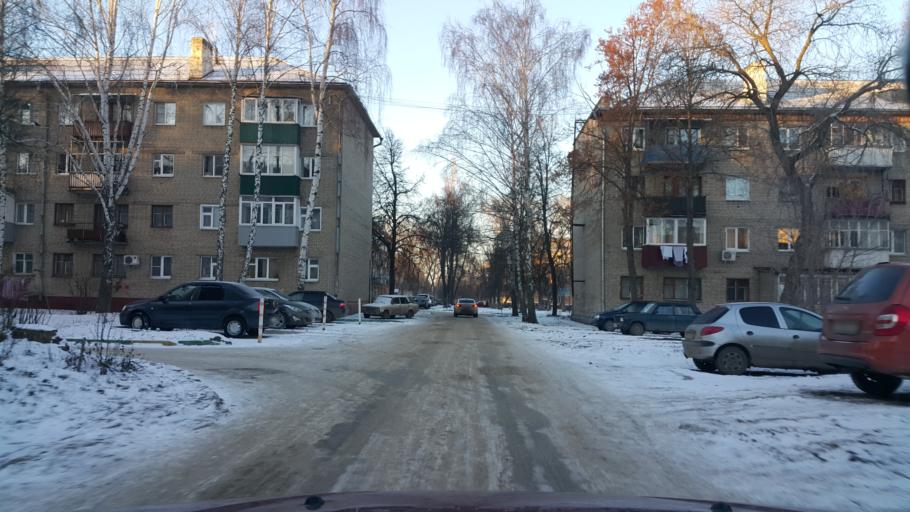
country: RU
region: Tambov
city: Pokrovo-Prigorodnoye
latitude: 52.7070
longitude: 41.3947
